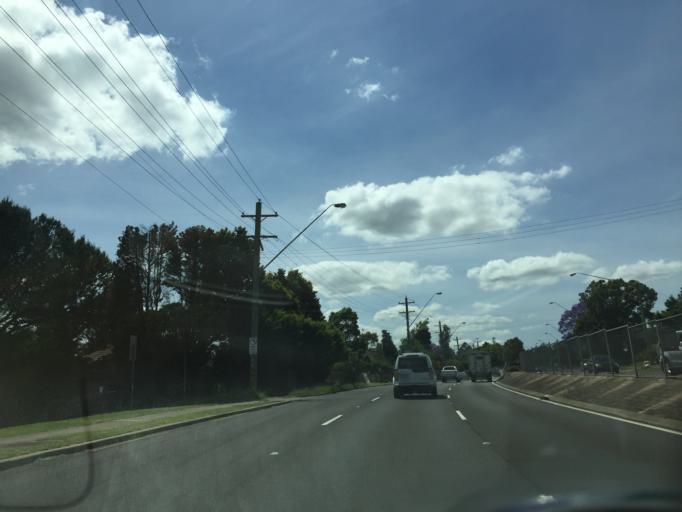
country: AU
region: New South Wales
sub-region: Parramatta
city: Dundas Valley
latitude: -33.7983
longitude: 151.0494
